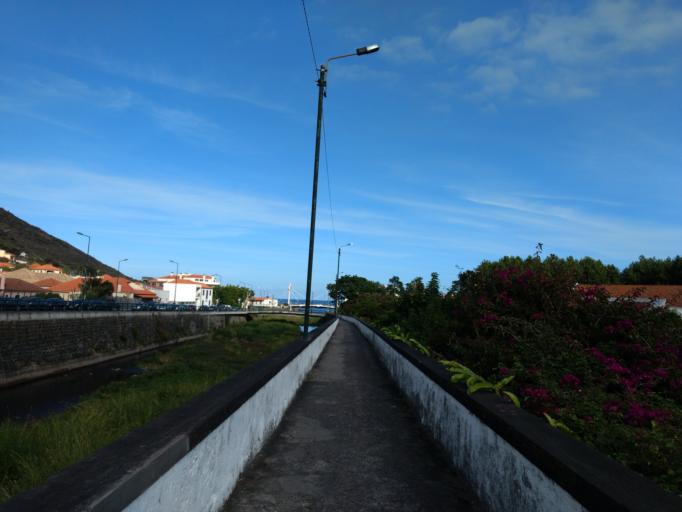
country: PT
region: Madeira
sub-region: Machico
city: Machico
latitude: 32.7197
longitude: -16.7666
